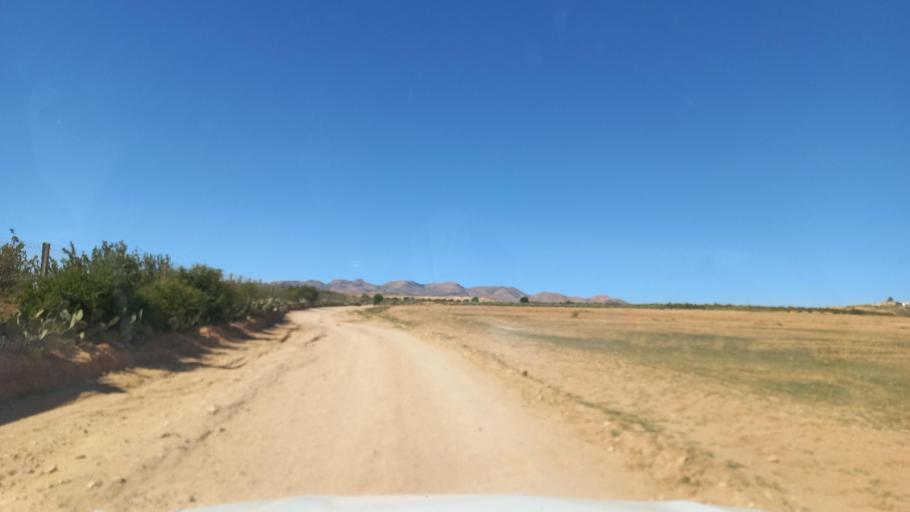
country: TN
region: Al Qasrayn
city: Sbiba
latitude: 35.3714
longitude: 9.0946
